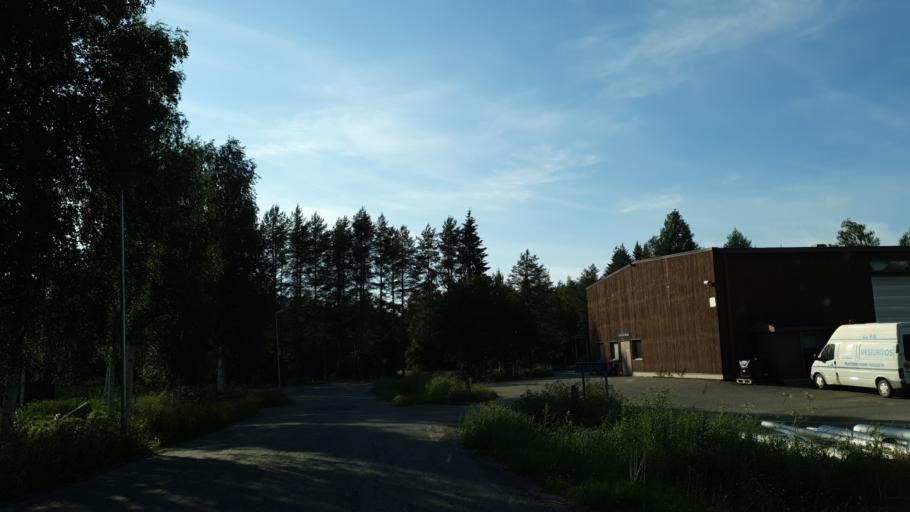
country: FI
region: Kainuu
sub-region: Kehys-Kainuu
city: Kuhmo
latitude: 64.1231
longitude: 29.5034
